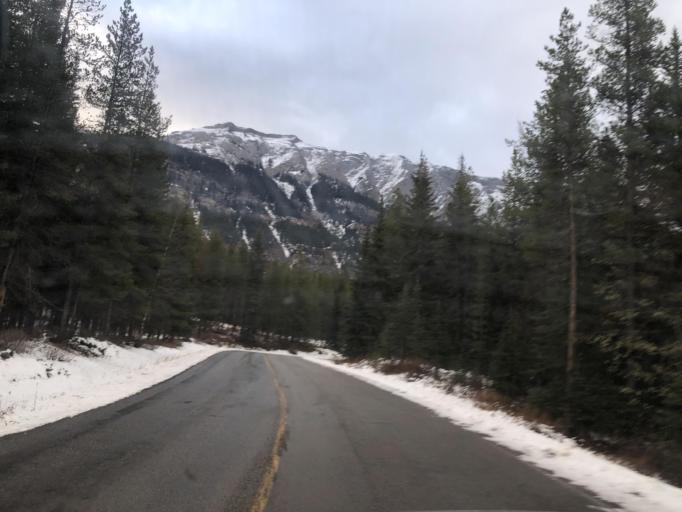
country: CA
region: Alberta
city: Canmore
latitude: 50.7107
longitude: -115.1155
